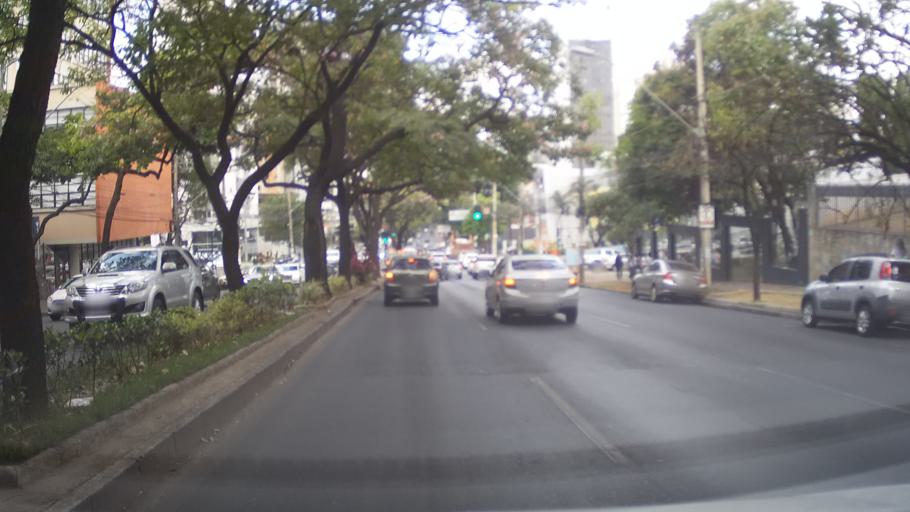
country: BR
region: Minas Gerais
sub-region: Belo Horizonte
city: Belo Horizonte
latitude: -19.9348
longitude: -43.9493
